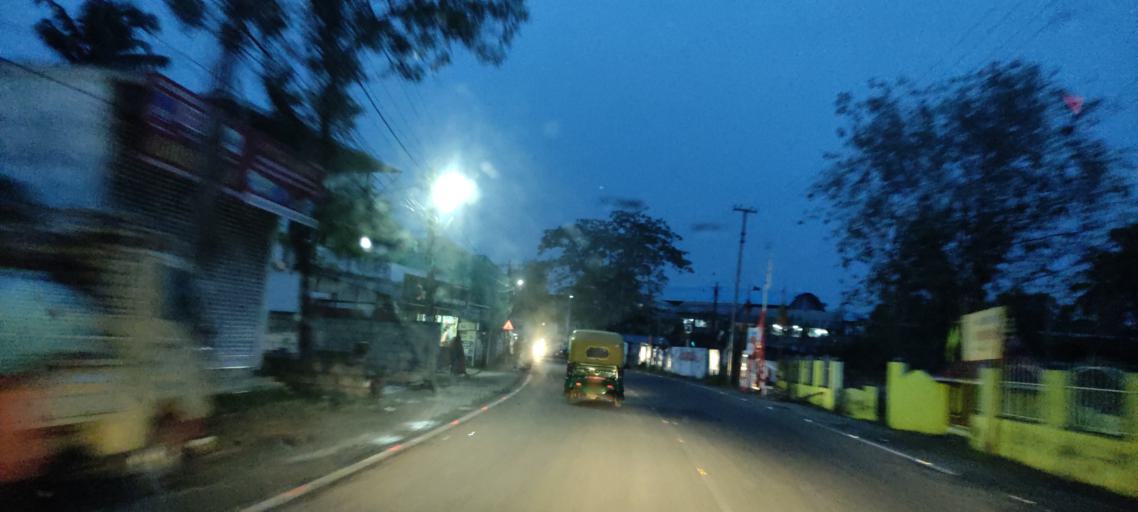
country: IN
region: Kerala
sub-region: Alappuzha
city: Arukutti
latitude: 9.8862
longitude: 76.2989
